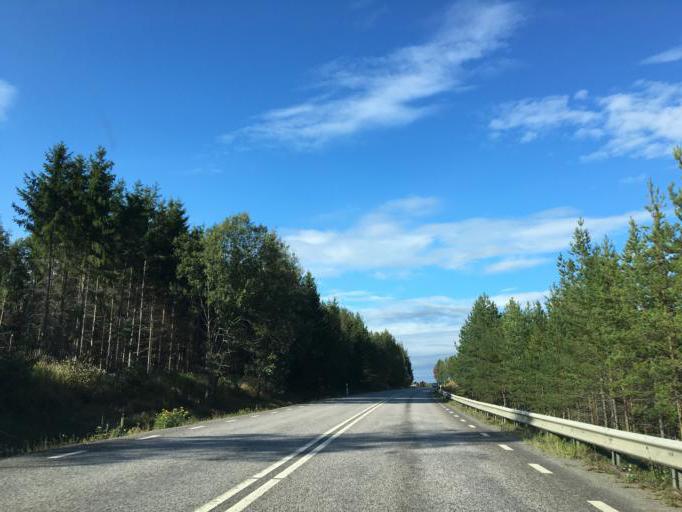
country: SE
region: Soedermanland
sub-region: Nykopings Kommun
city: Svalsta
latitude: 58.8539
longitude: 16.9185
